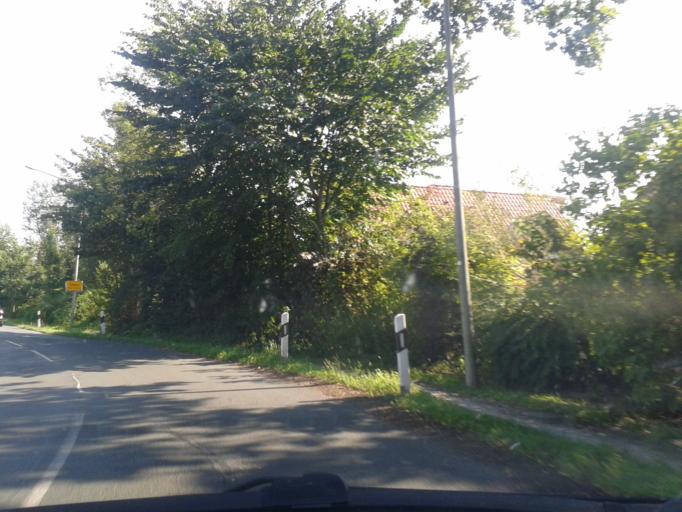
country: DE
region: North Rhine-Westphalia
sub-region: Regierungsbezirk Detmold
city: Hovelhof
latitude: 51.7452
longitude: 8.6698
